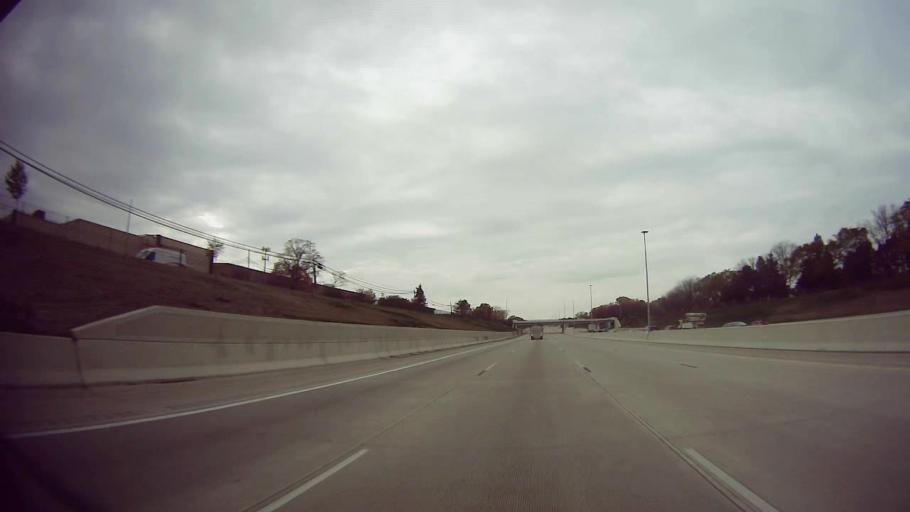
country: US
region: Michigan
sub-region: Wayne County
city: Livonia
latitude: 42.3823
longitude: -83.3830
